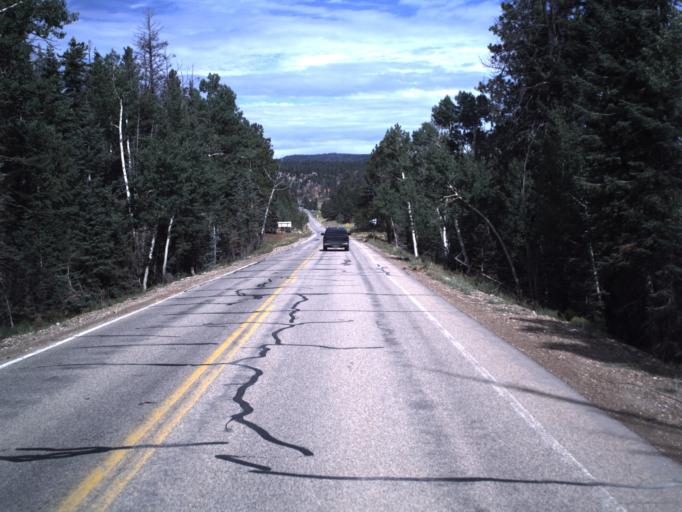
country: US
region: Utah
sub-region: Iron County
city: Parowan
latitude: 37.5191
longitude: -112.6490
